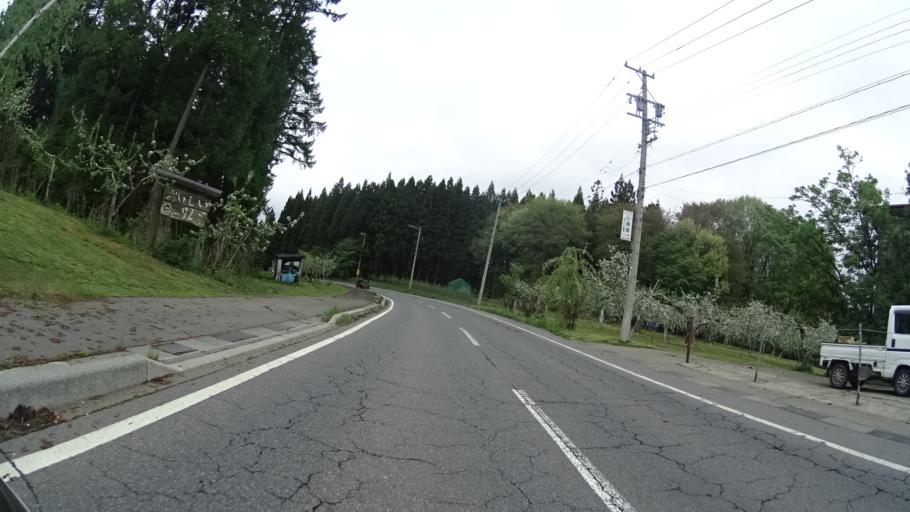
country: JP
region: Nagano
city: Nagano-shi
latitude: 36.7262
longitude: 138.2098
